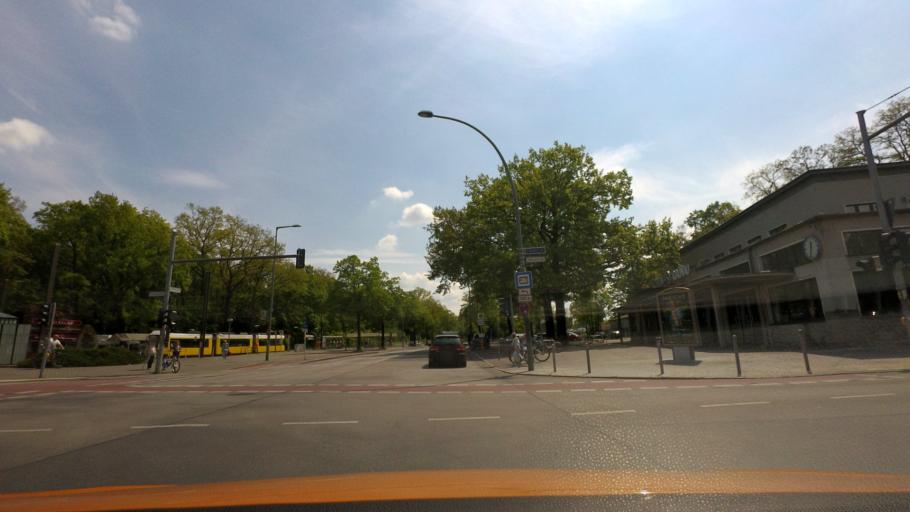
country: DE
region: Berlin
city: Grunau
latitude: 52.4136
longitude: 13.5736
